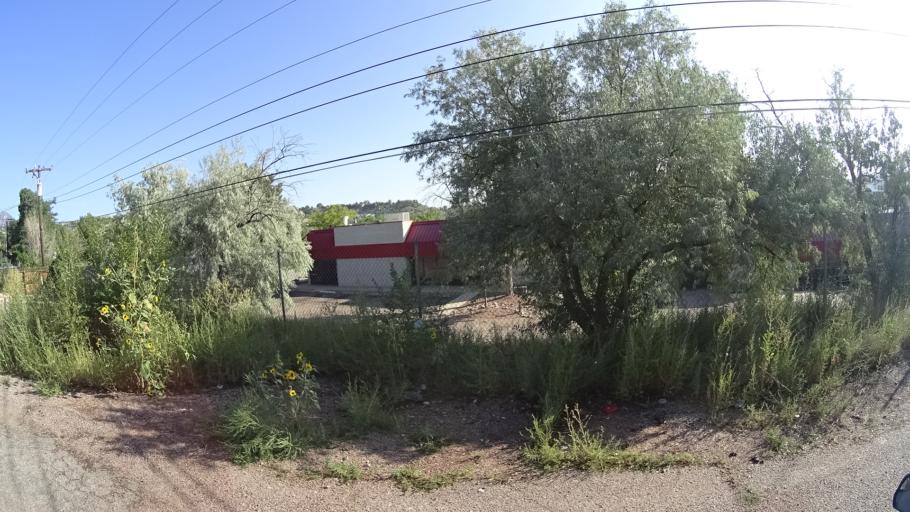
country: US
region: Colorado
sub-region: El Paso County
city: Colorado Springs
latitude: 38.8935
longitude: -104.8349
